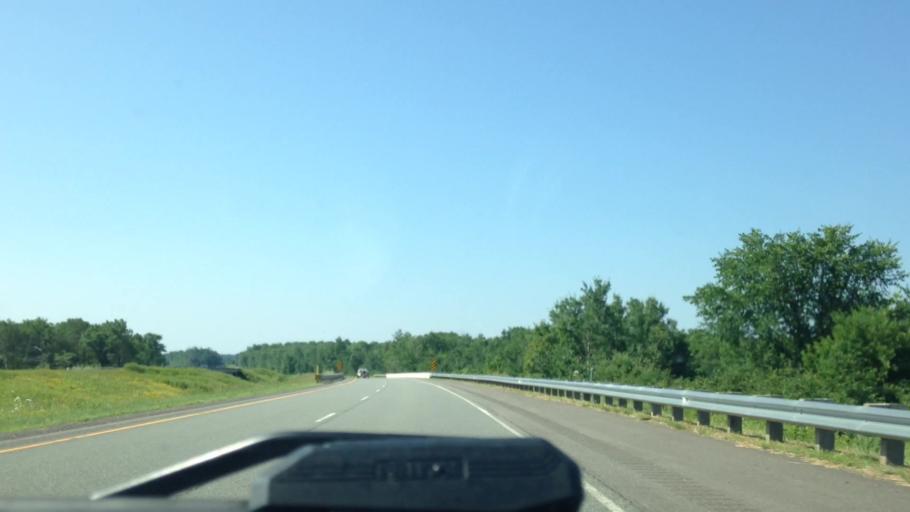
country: US
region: Wisconsin
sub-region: Douglas County
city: Lake Nebagamon
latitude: 46.3994
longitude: -91.8179
